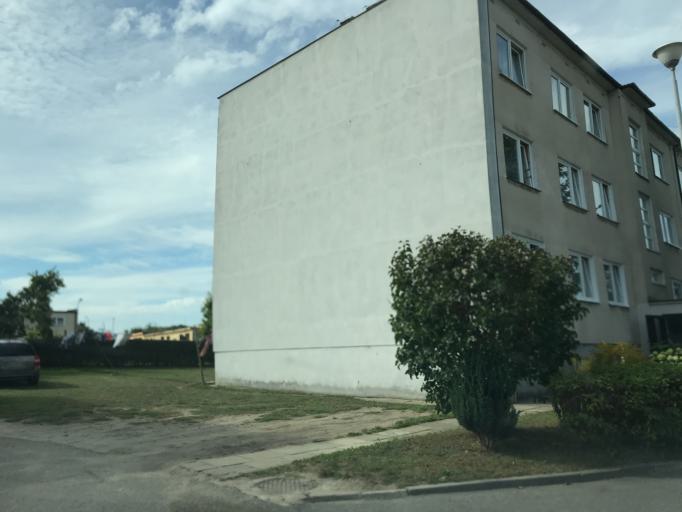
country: PL
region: Pomeranian Voivodeship
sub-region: Powiat pucki
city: Krokowa
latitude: 54.7815
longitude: 18.1586
